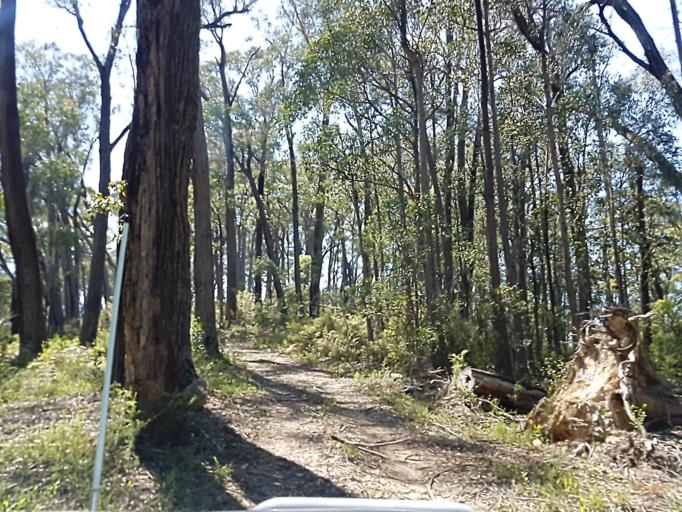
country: AU
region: Victoria
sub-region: East Gippsland
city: Lakes Entrance
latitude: -37.3147
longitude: 148.3405
